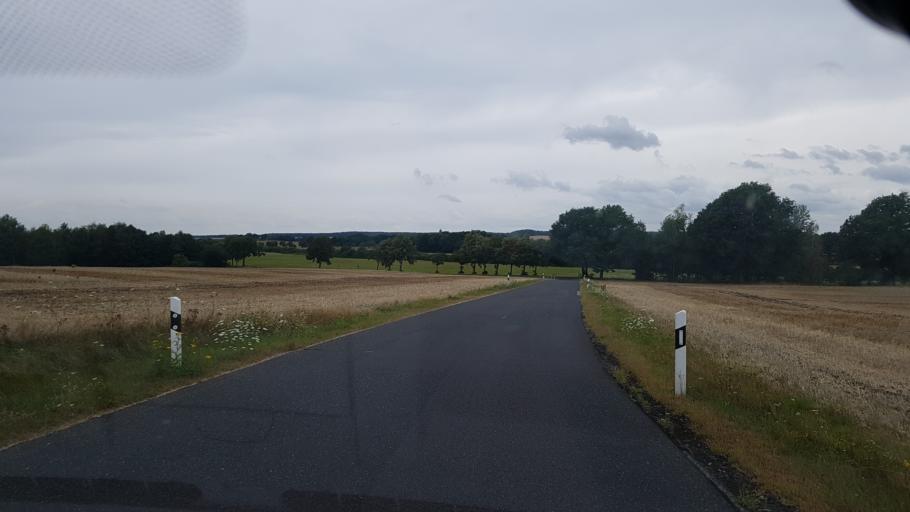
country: DE
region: Saxony
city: Reichenbach
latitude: 51.2135
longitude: 14.7983
